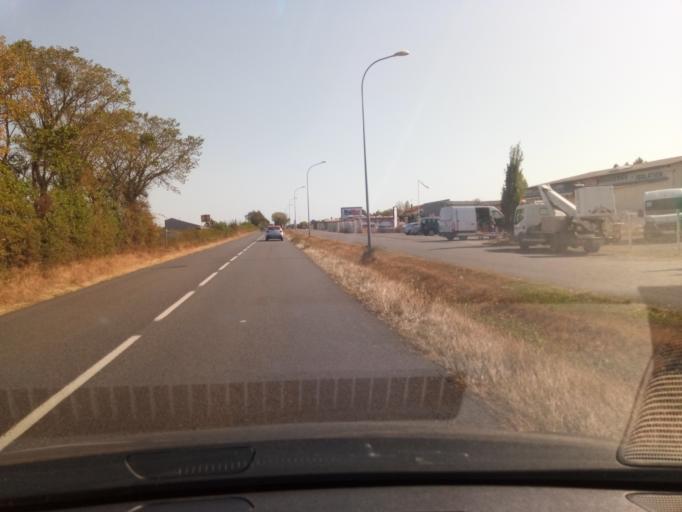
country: FR
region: Poitou-Charentes
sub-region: Departement de la Vienne
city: Montmorillon
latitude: 46.4328
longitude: 0.8970
